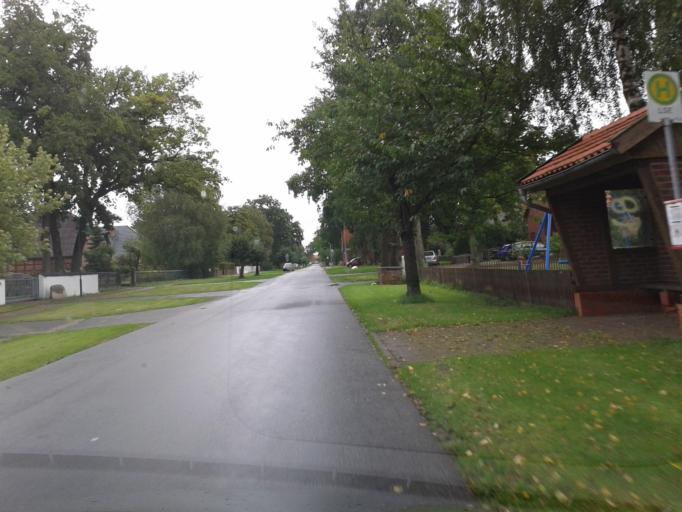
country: DE
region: Lower Saxony
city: Woltersdorf
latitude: 52.9521
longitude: 11.2154
